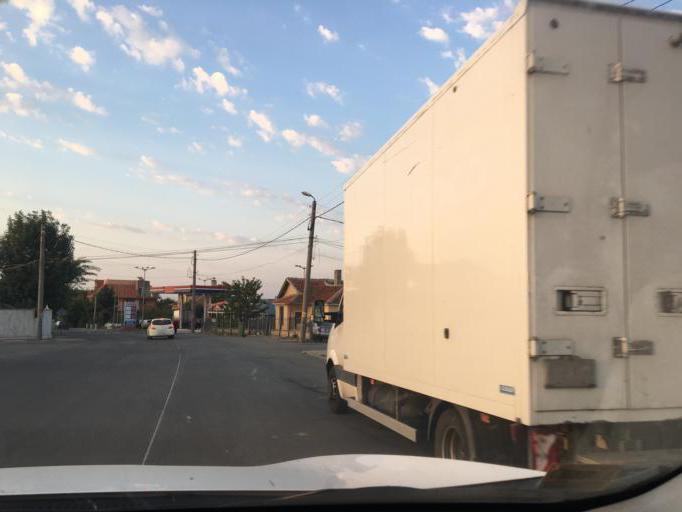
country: BG
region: Burgas
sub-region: Obshtina Burgas
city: Burgas
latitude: 42.6128
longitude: 27.4929
